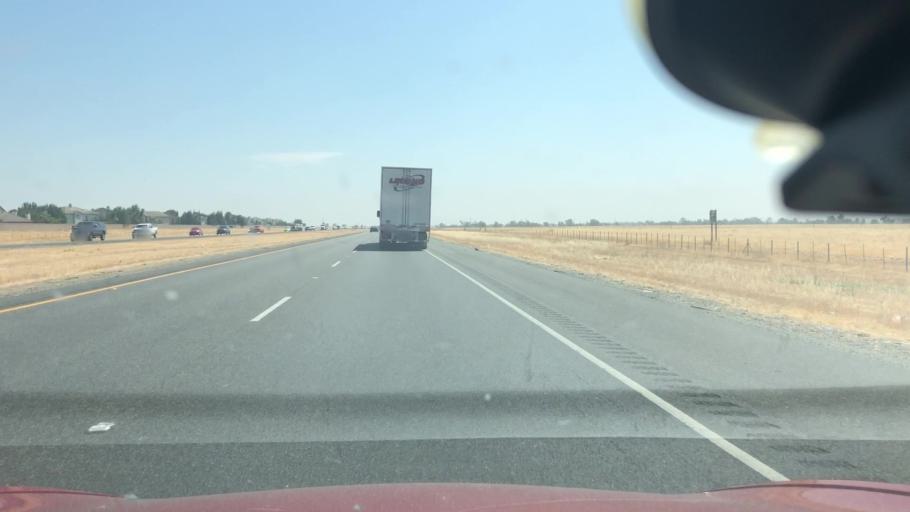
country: US
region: California
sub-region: Sacramento County
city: Laguna
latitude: 38.4020
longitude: -121.4826
